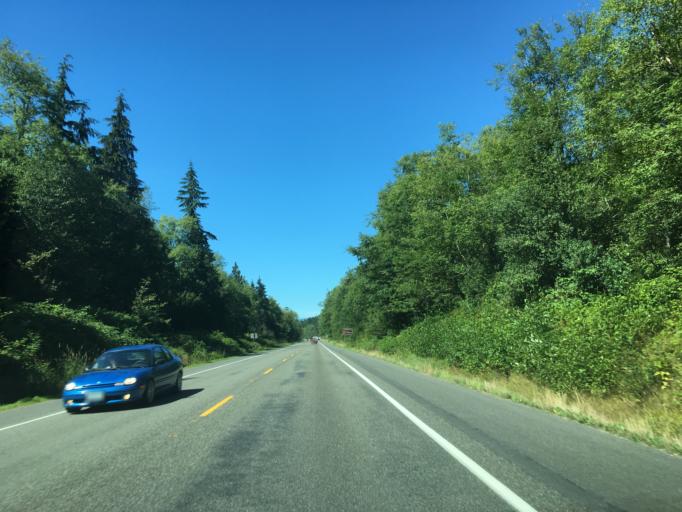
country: US
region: Washington
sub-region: Snohomish County
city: Sisco Heights
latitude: 48.1441
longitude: -122.1130
